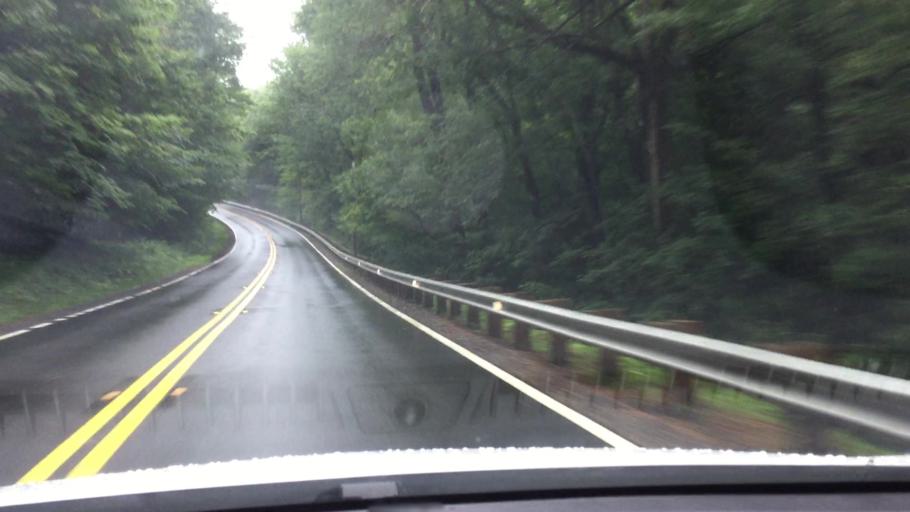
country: US
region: Massachusetts
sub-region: Berkshire County
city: Becket
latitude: 42.3461
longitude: -73.1182
